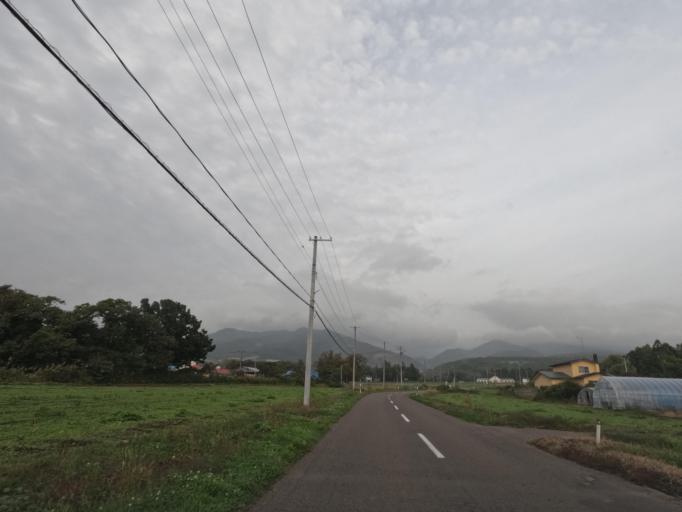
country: JP
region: Hokkaido
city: Date
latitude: 42.4259
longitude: 140.9125
